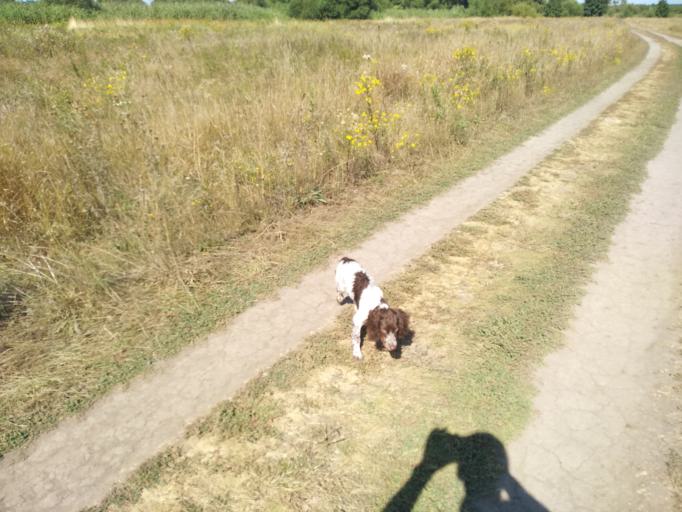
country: RU
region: Voronezj
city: Novaya Usman'
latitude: 51.6625
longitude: 39.3700
